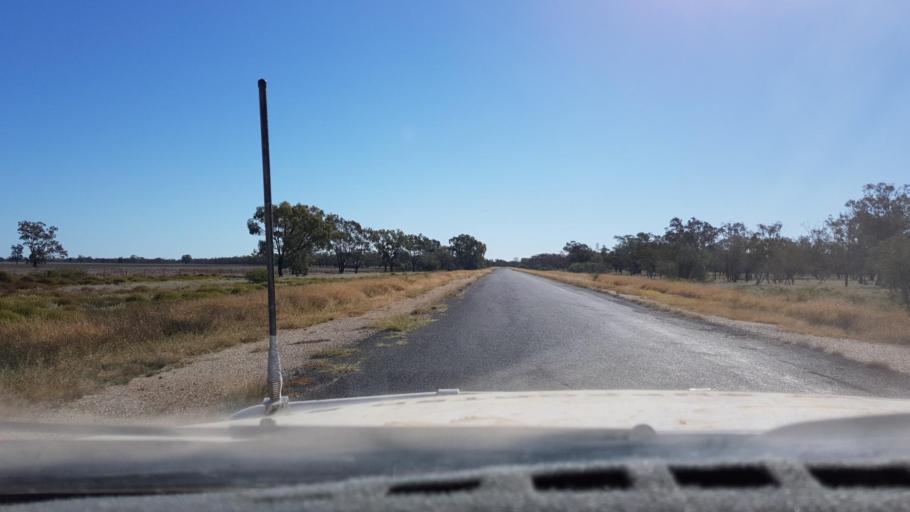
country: AU
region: New South Wales
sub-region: Walgett
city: Lightning Ridge
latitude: -29.5738
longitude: 148.6723
